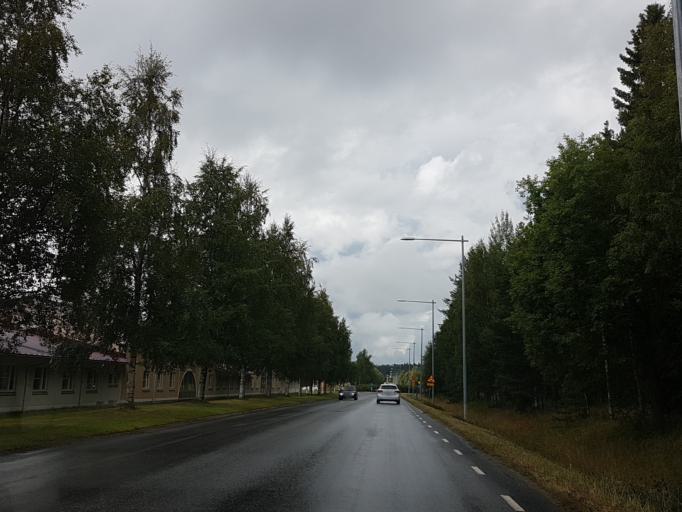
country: SE
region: Vaesterbotten
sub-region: Umea Kommun
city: Ersmark
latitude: 63.8520
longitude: 20.3193
